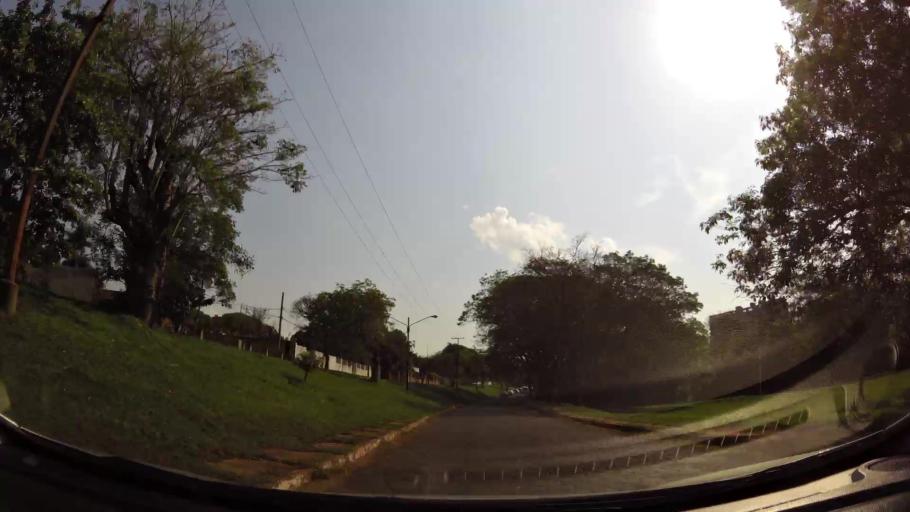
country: PY
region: Alto Parana
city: Presidente Franco
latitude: -25.5157
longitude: -54.6392
